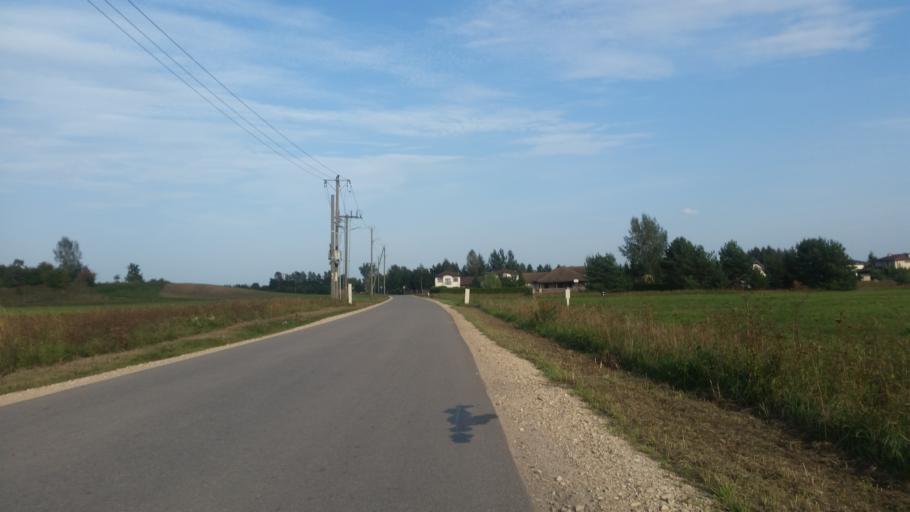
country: LV
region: Ikskile
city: Ikskile
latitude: 56.8183
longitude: 24.5176
